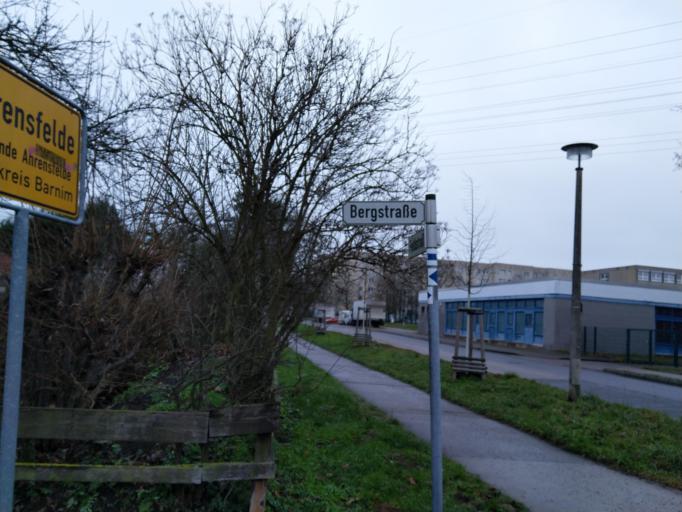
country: DE
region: Brandenburg
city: Ahrensfelde
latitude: 52.5720
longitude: 13.5774
